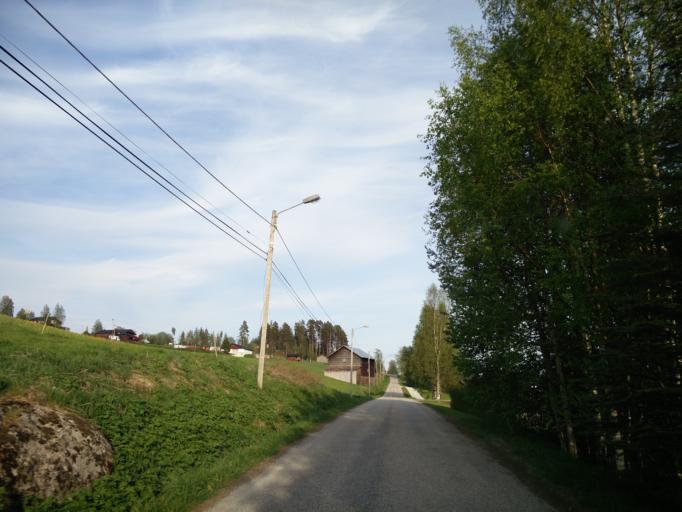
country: SE
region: Jaemtland
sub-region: Bergs Kommun
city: Hoverberg
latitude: 62.5637
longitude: 14.3808
